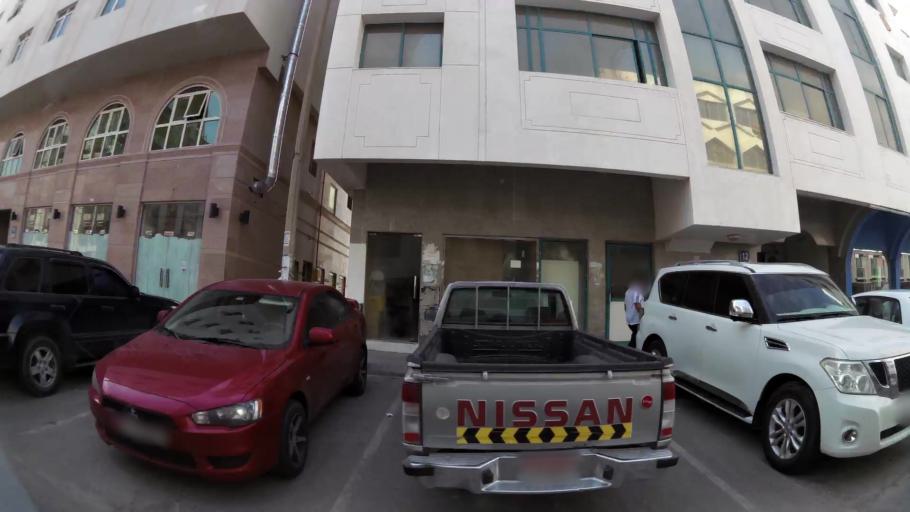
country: AE
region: Abu Dhabi
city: Abu Dhabi
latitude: 24.3274
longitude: 54.5310
